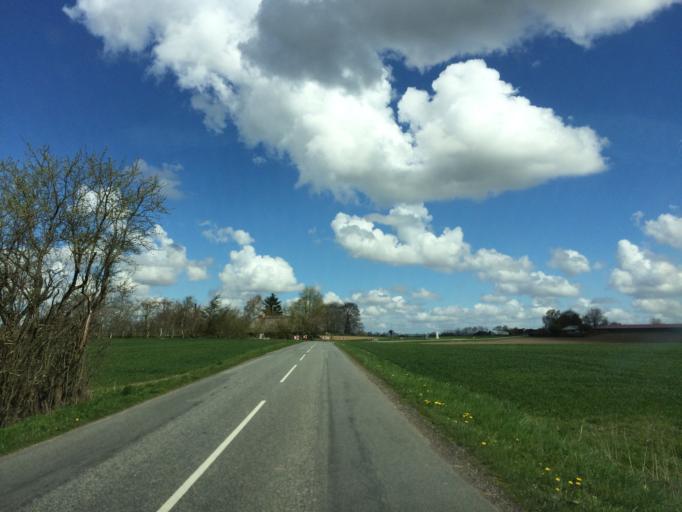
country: DK
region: South Denmark
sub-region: Odense Kommune
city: Bellinge
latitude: 55.2621
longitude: 10.2903
